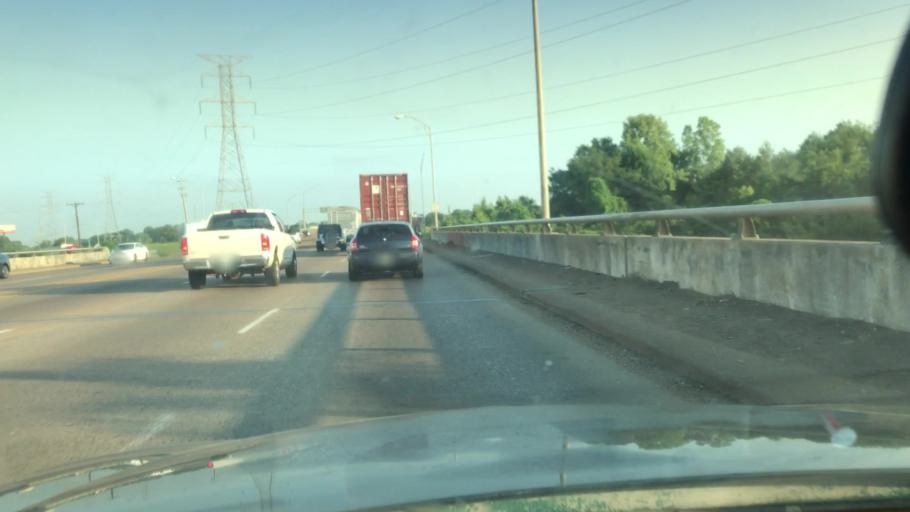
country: US
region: Tennessee
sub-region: Shelby County
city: New South Memphis
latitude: 35.0779
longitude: -89.9526
